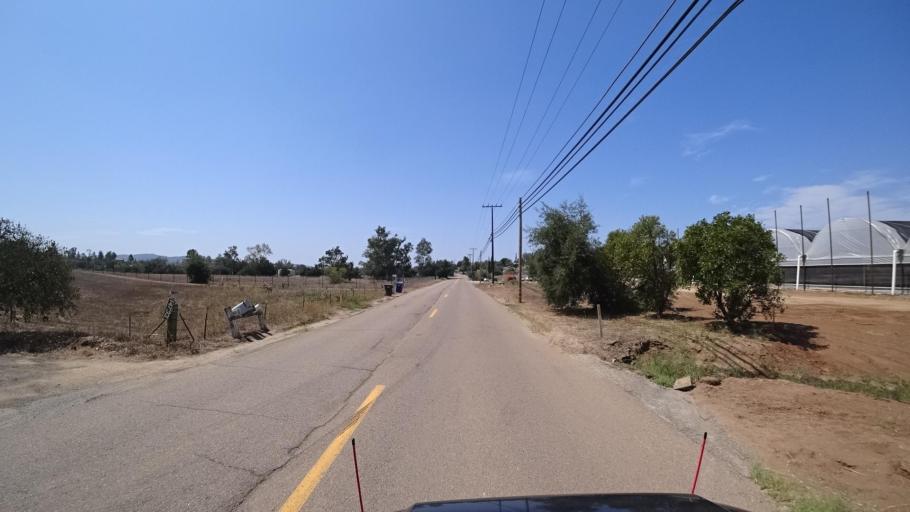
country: US
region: California
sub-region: San Diego County
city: Valley Center
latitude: 33.2423
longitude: -117.0118
